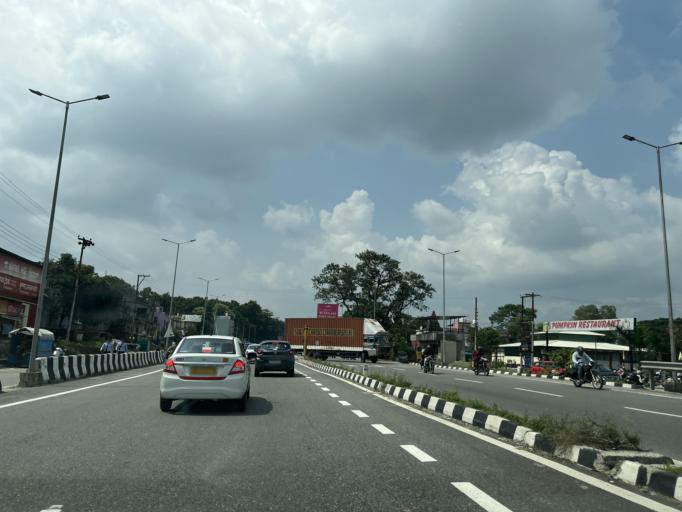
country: IN
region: Uttarakhand
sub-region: Dehradun
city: Raipur
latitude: 30.2460
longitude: 78.0978
